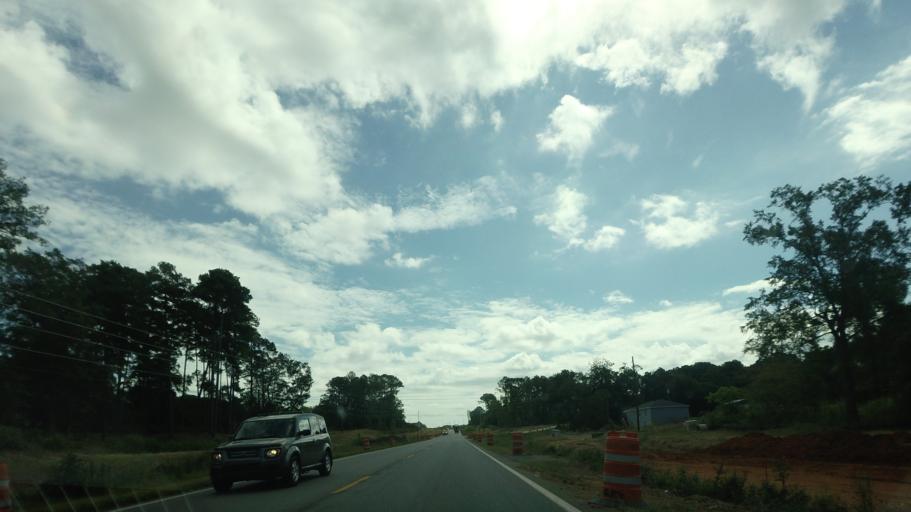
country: US
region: Georgia
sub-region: Houston County
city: Robins Air Force Base
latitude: 32.5521
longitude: -83.6121
